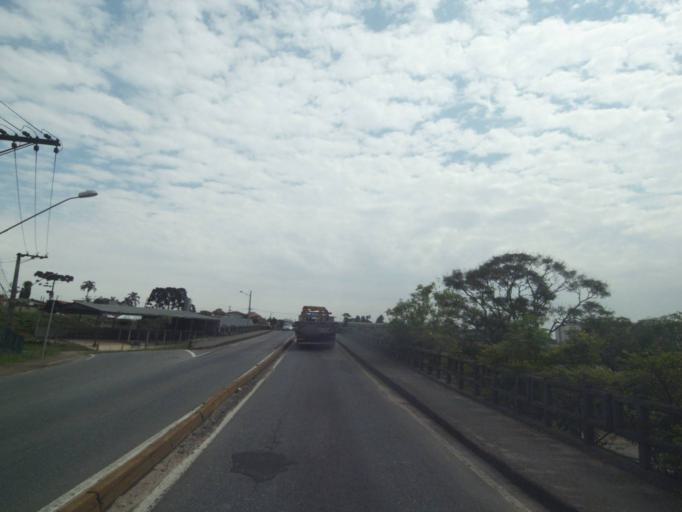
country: BR
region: Parana
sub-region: Pinhais
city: Pinhais
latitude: -25.3944
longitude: -49.2096
